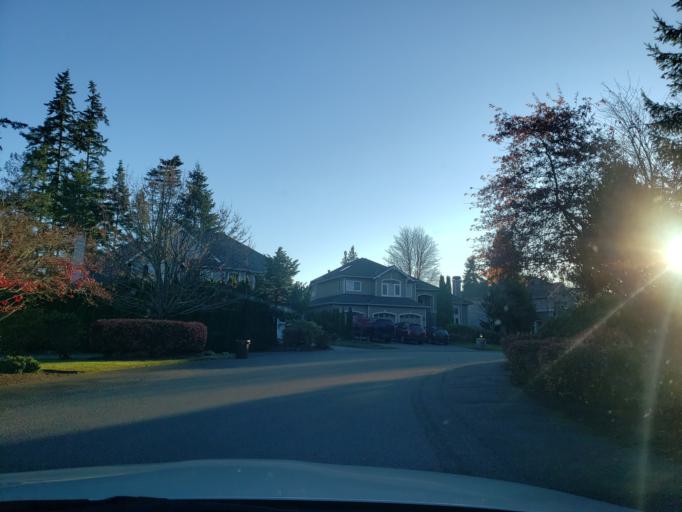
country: US
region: Washington
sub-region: Snohomish County
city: Woodway
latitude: 47.7786
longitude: -122.3782
